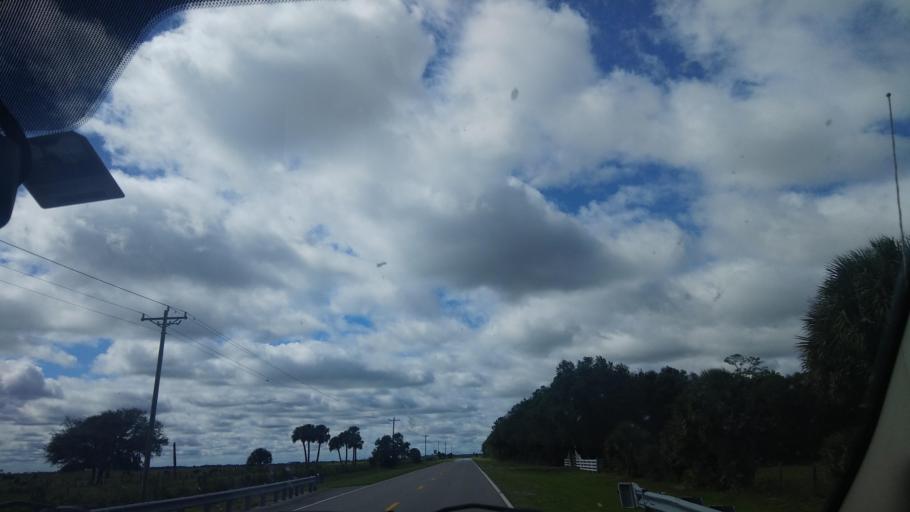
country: US
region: Florida
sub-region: Okeechobee County
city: Okeechobee
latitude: 27.3930
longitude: -80.9223
